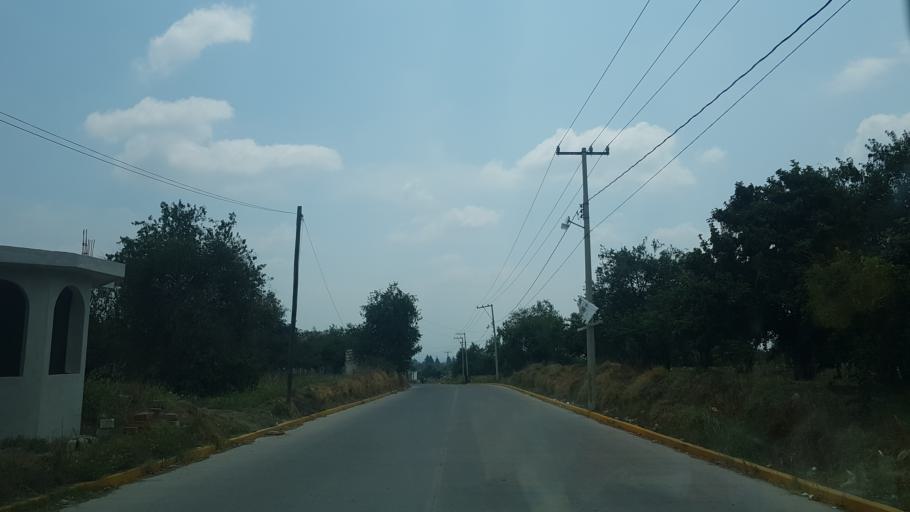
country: MX
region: Puebla
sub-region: Huejotzingo
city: San Juan Pancoac
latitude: 19.1387
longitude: -98.4382
